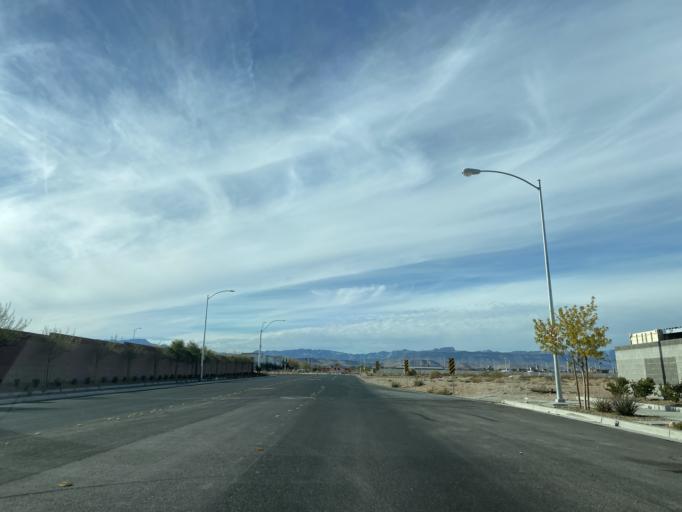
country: US
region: Nevada
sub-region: Clark County
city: Enterprise
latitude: 36.0617
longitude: -115.2323
